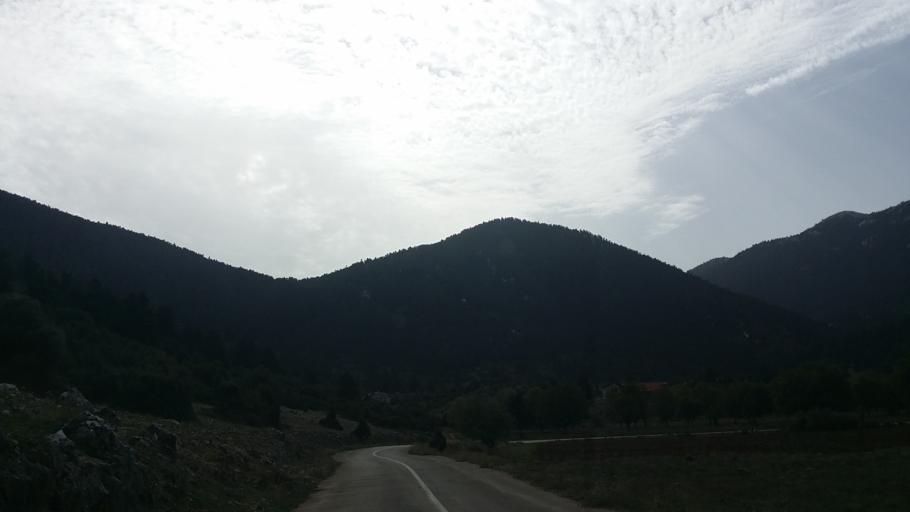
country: GR
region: Central Greece
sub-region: Nomos Voiotias
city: Kyriaki
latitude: 38.3720
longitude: 22.8471
